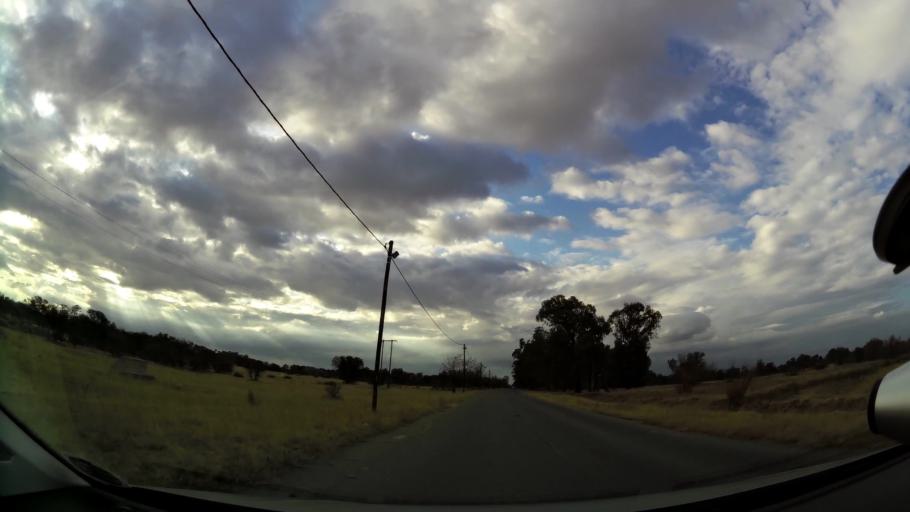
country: ZA
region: Orange Free State
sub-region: Lejweleputswa District Municipality
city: Welkom
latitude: -28.0066
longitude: 26.7100
